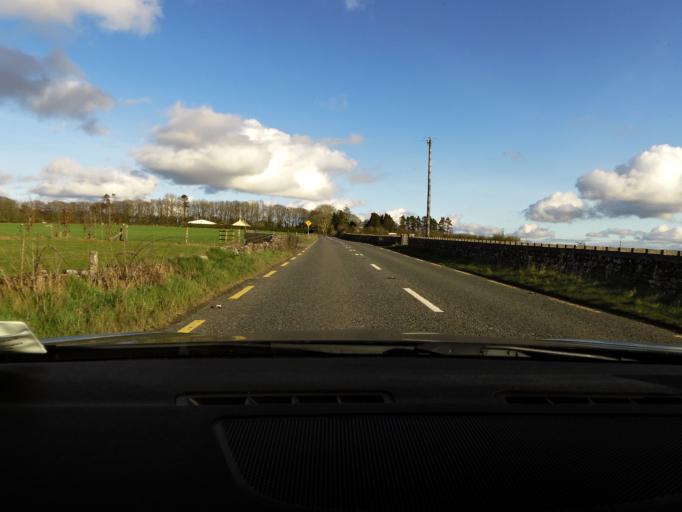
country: IE
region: Connaught
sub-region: Roscommon
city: Castlerea
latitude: 53.6801
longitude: -8.3513
